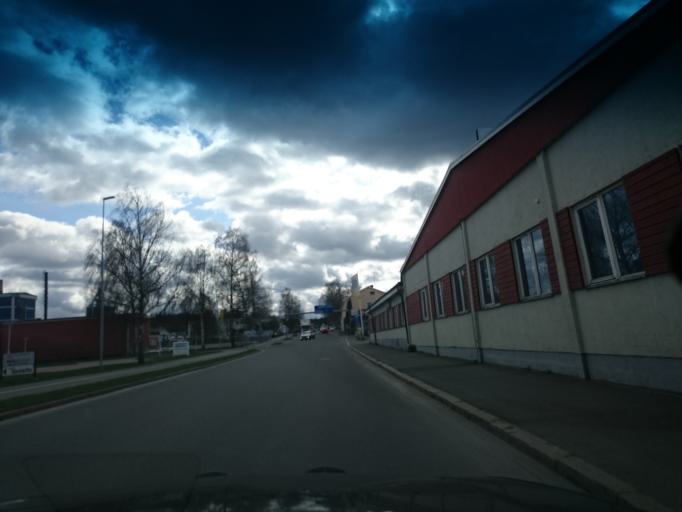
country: SE
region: Joenkoeping
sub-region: Vetlanda Kommun
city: Vetlanda
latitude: 57.4225
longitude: 15.0826
